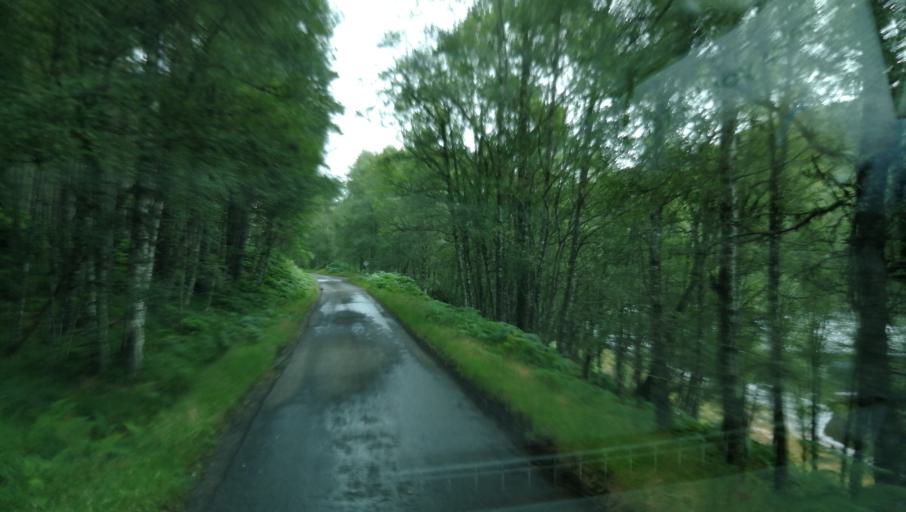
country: GB
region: Scotland
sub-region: Highland
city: Spean Bridge
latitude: 57.3054
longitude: -4.8736
